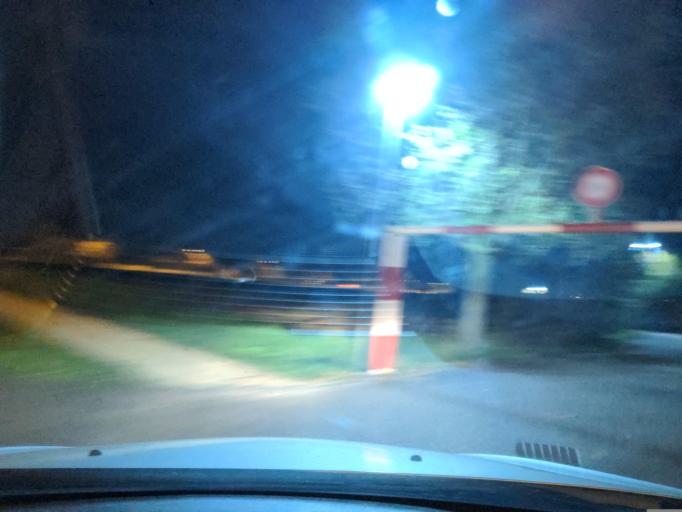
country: FR
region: Bourgogne
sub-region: Departement de la Cote-d'Or
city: Saint-Apollinaire
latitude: 47.3282
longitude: 5.0855
